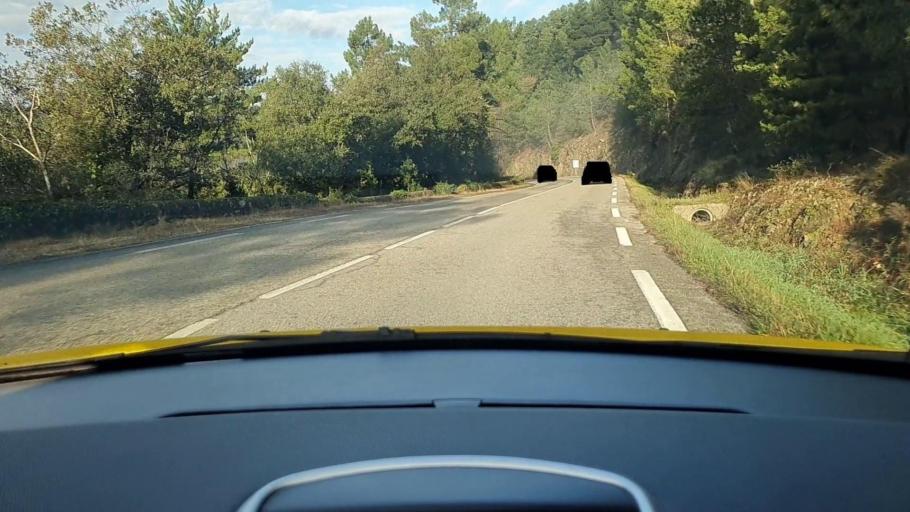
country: FR
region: Languedoc-Roussillon
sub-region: Departement du Gard
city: Branoux-les-Taillades
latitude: 44.2843
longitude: 3.9924
